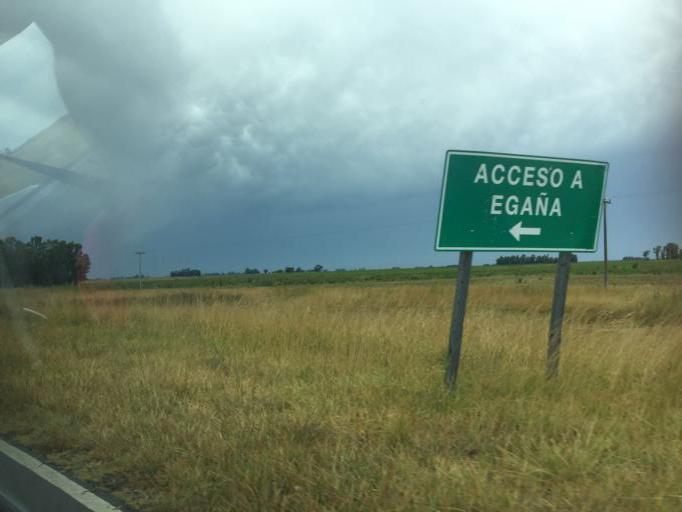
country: AR
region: Buenos Aires
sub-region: Partido de Rauch
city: Rauch
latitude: -36.9146
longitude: -58.9865
